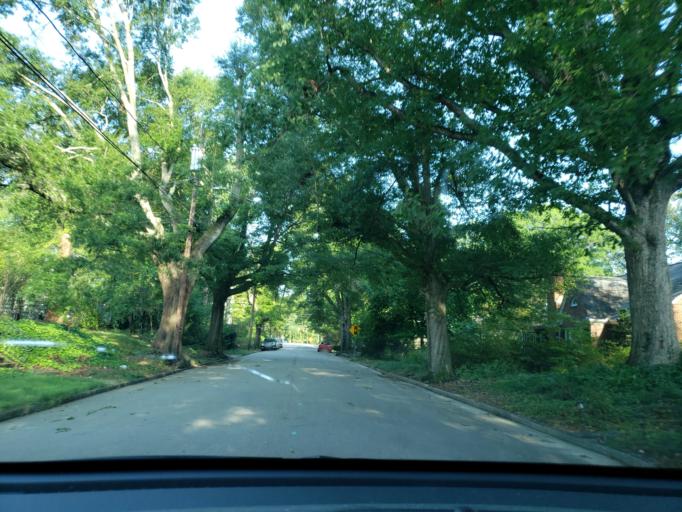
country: US
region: North Carolina
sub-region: Durham County
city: Durham
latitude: 35.9767
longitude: -78.9154
